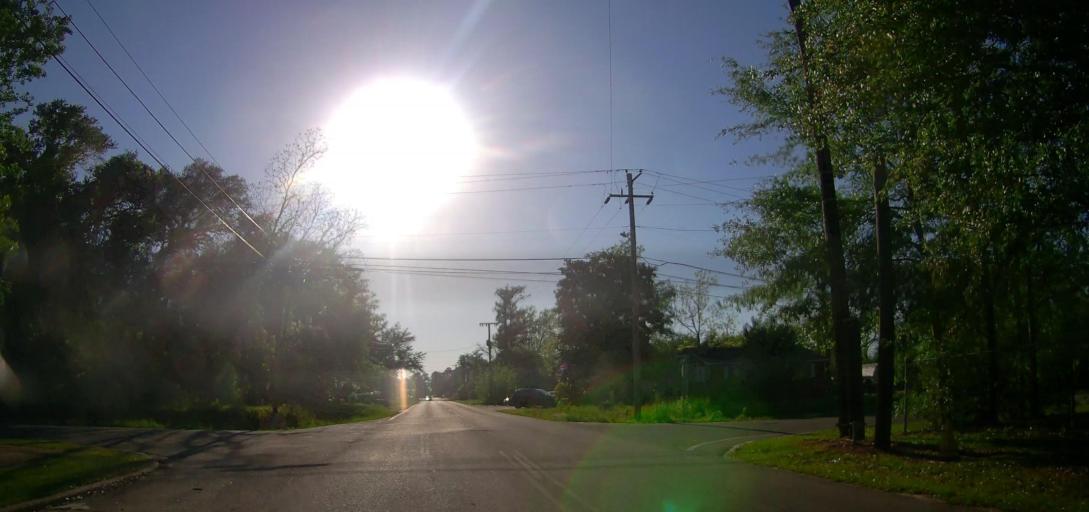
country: US
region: Georgia
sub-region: Ben Hill County
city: Fitzgerald
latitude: 31.7059
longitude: -83.2488
